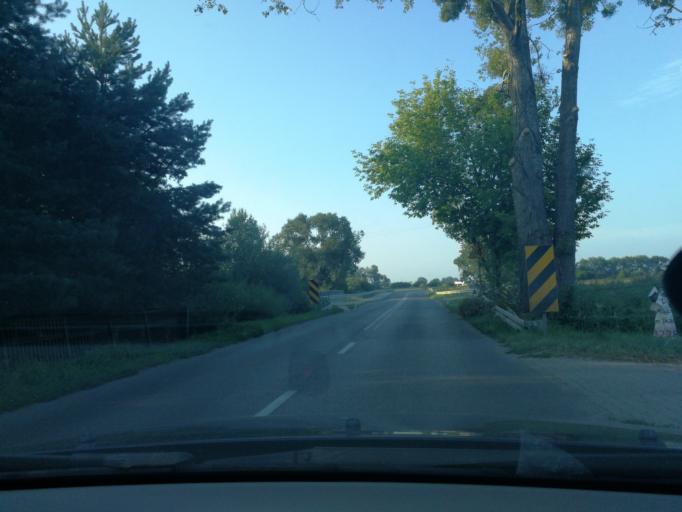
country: PL
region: Masovian Voivodeship
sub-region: Powiat pruszkowski
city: Brwinow
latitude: 52.1547
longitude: 20.7304
